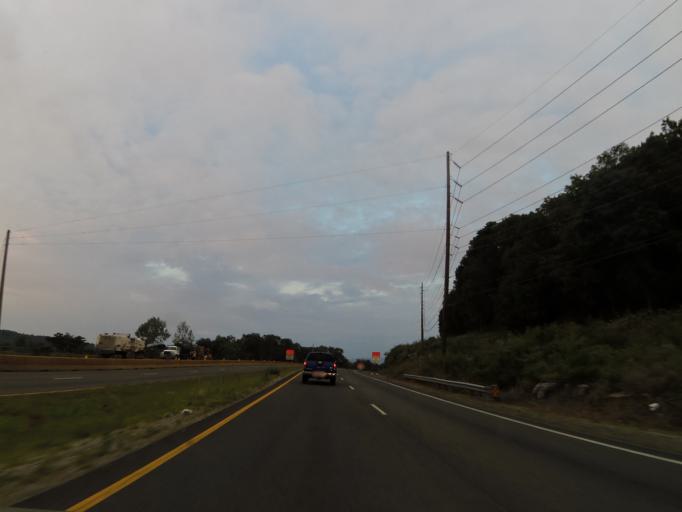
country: US
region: Alabama
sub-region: Madison County
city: Huntsville
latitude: 34.7719
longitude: -86.5486
